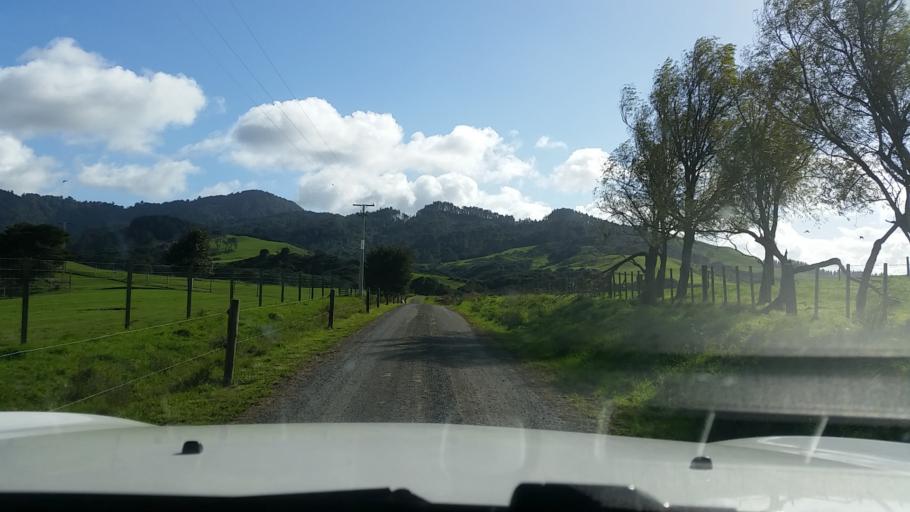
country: NZ
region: Waikato
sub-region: Hauraki District
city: Ngatea
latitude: -37.4991
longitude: 175.4038
